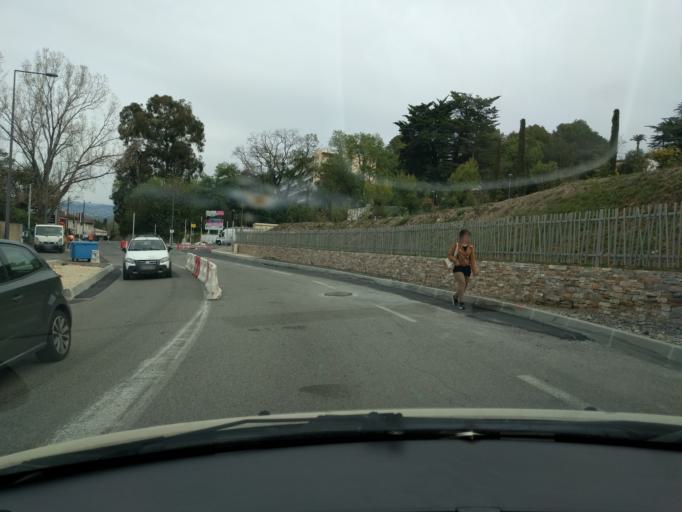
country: FR
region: Provence-Alpes-Cote d'Azur
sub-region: Departement des Alpes-Maritimes
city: La Roquette-sur-Siagne
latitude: 43.5712
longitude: 6.9552
